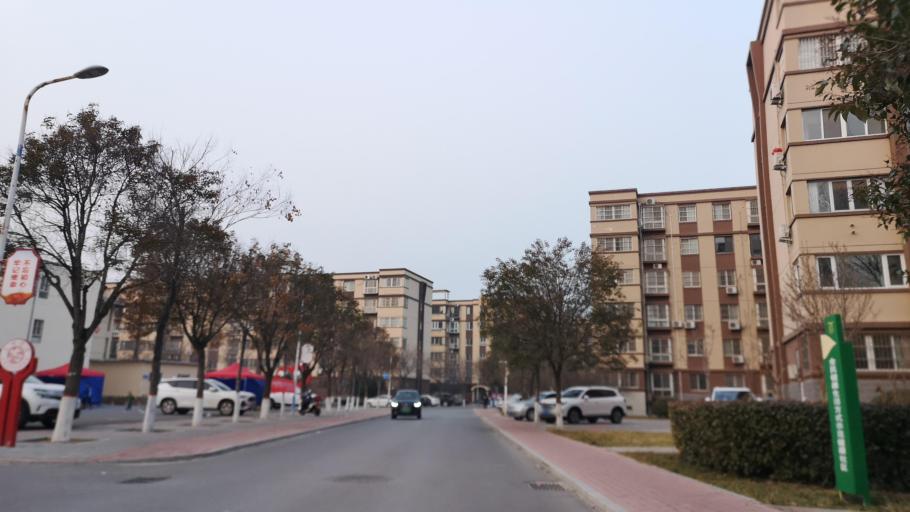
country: CN
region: Henan Sheng
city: Zhongyuanlu
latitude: 35.7867
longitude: 115.0782
